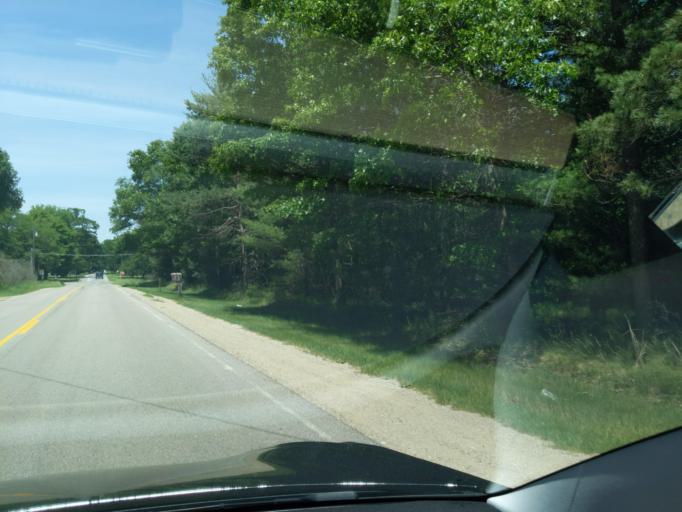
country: US
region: Michigan
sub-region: Muskegon County
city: Montague
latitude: 43.4147
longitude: -86.4167
